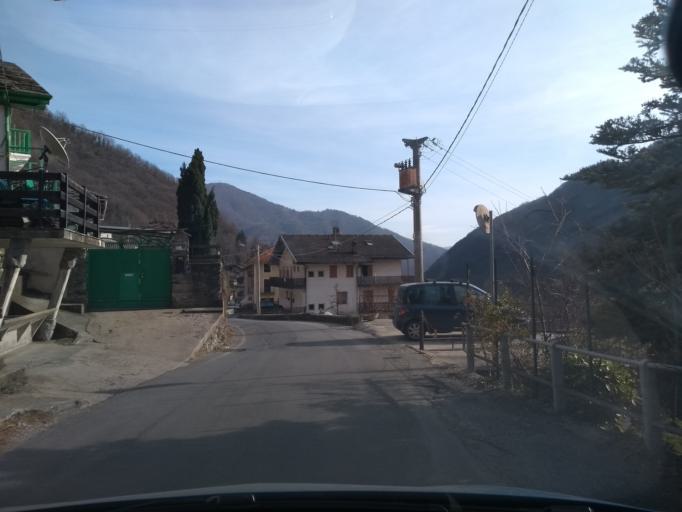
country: IT
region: Piedmont
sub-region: Provincia di Torino
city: Ceres
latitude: 45.3190
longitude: 7.3703
